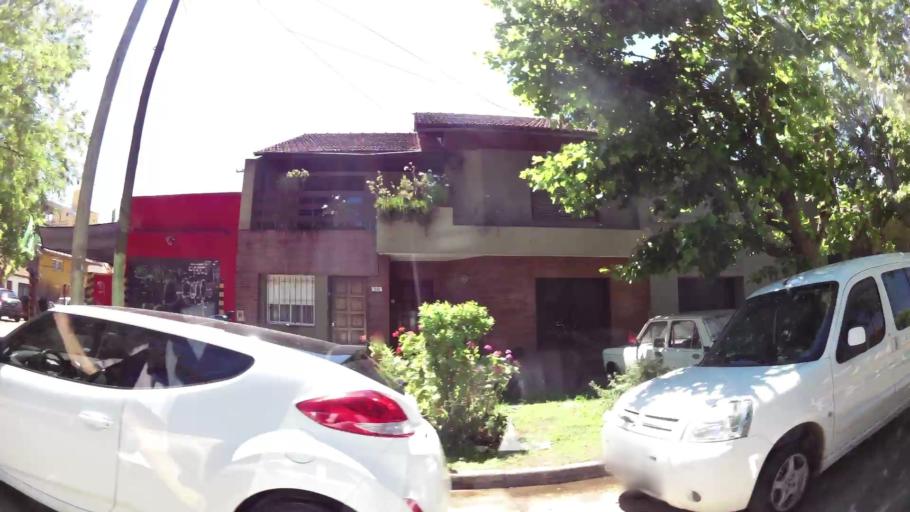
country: AR
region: Buenos Aires
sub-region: Partido de Quilmes
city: Quilmes
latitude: -34.7253
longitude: -58.2630
